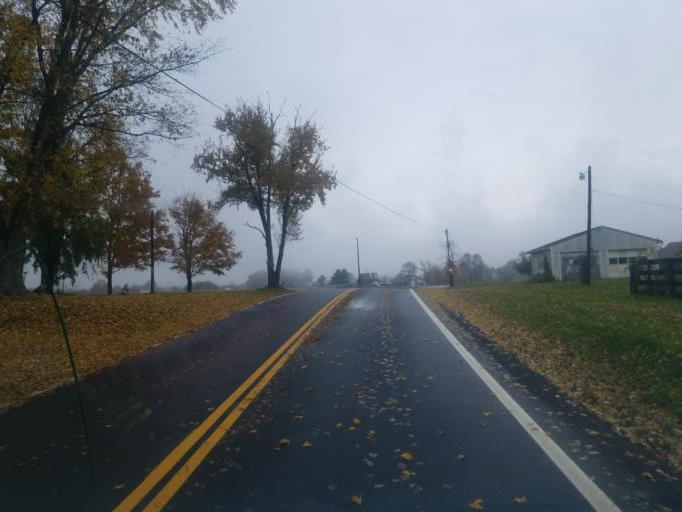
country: US
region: Ohio
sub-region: Morgan County
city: McConnelsville
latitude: 39.5500
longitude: -81.8221
